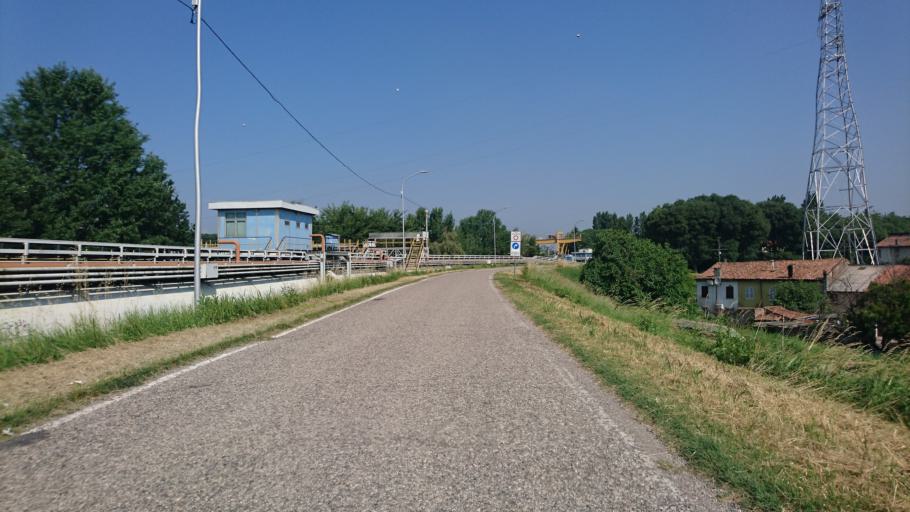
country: IT
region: Lombardy
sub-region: Provincia di Mantova
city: Ostiglia
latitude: 45.0608
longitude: 11.1338
